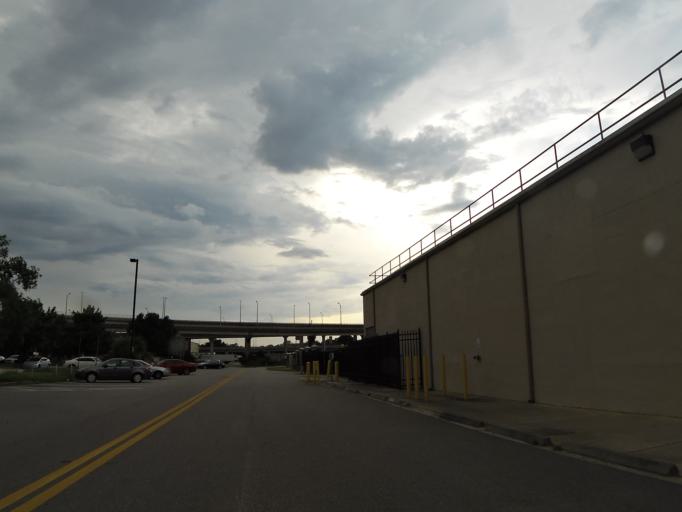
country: US
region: Florida
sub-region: Duval County
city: Jacksonville
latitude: 30.3246
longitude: -81.6491
